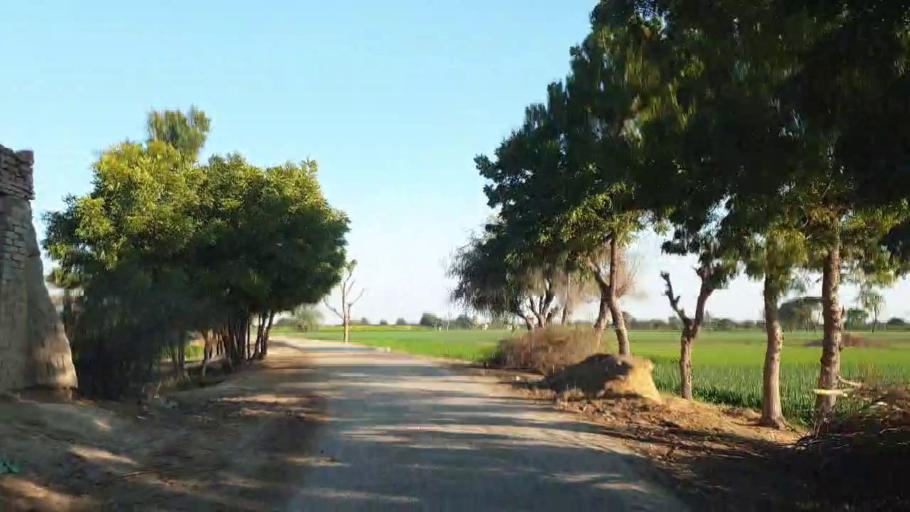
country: PK
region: Sindh
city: Shahpur Chakar
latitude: 26.1287
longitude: 68.5451
